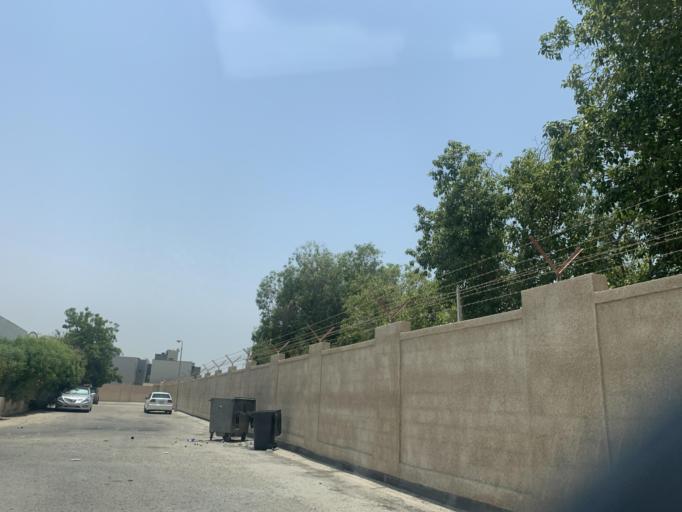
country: BH
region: Manama
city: Jidd Hafs
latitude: 26.2145
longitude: 50.4676
